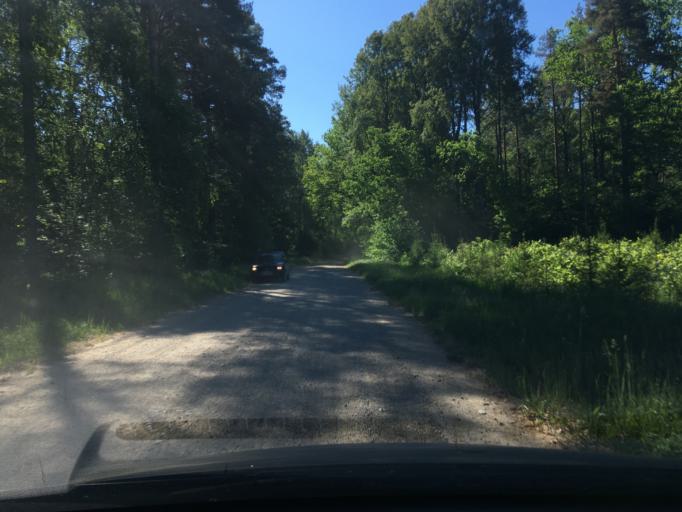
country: EE
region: Laeaene
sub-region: Lihula vald
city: Lihula
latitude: 58.6438
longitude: 23.7866
